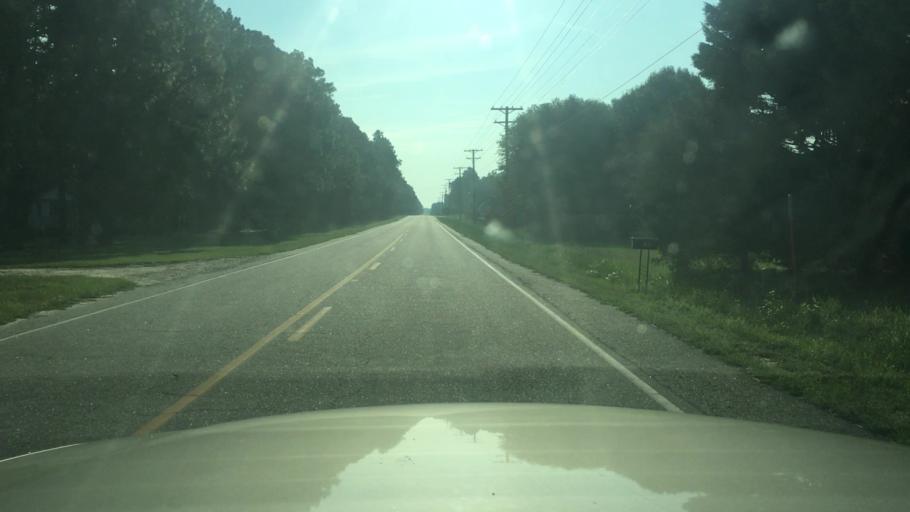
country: US
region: North Carolina
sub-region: Harnett County
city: Walkertown
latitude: 35.2076
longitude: -78.8704
